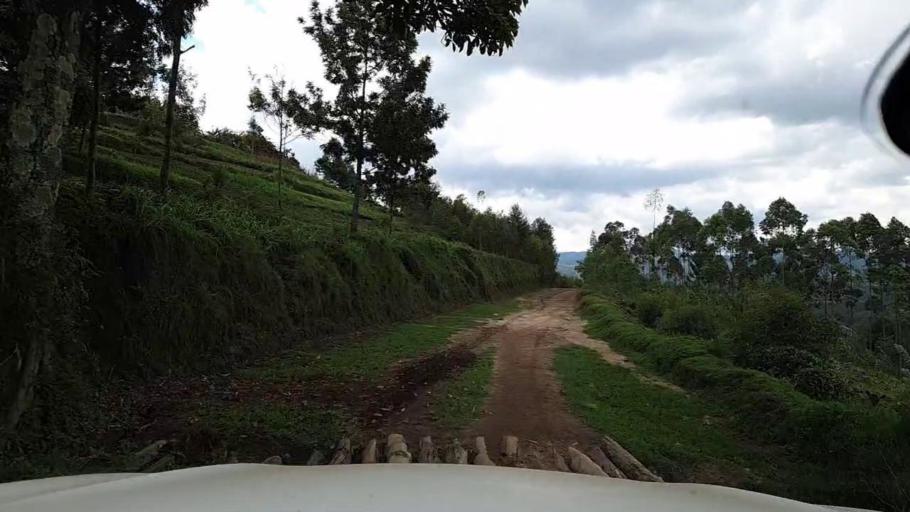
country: RW
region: Southern Province
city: Nzega
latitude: -2.6380
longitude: 29.4817
